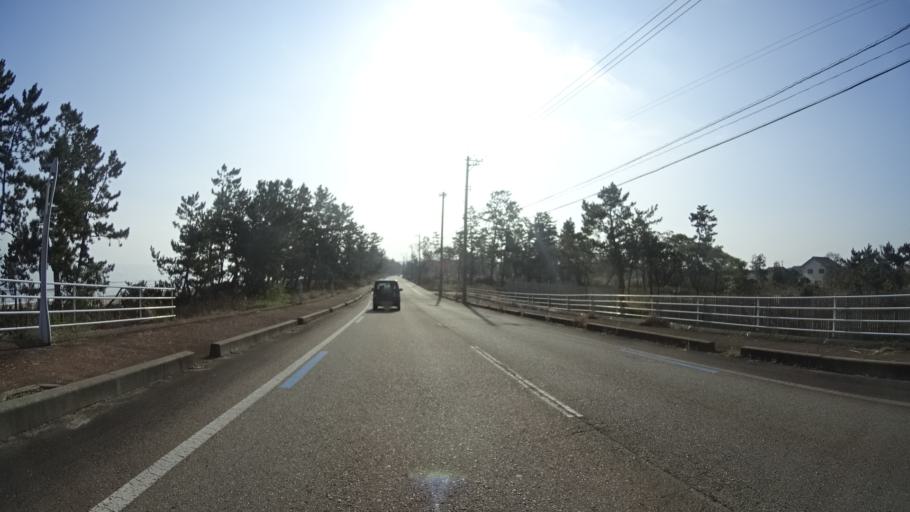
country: JP
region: Toyama
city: Himi
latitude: 36.8425
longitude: 136.9997
